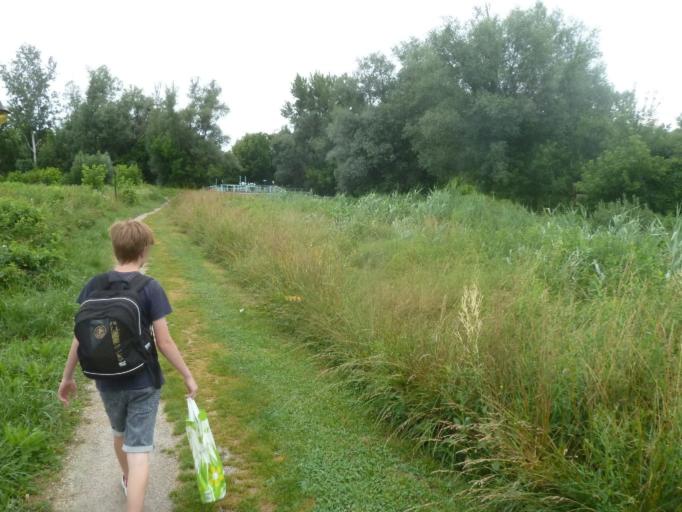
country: HU
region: Zala
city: Heviz
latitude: 46.7818
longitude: 17.1963
